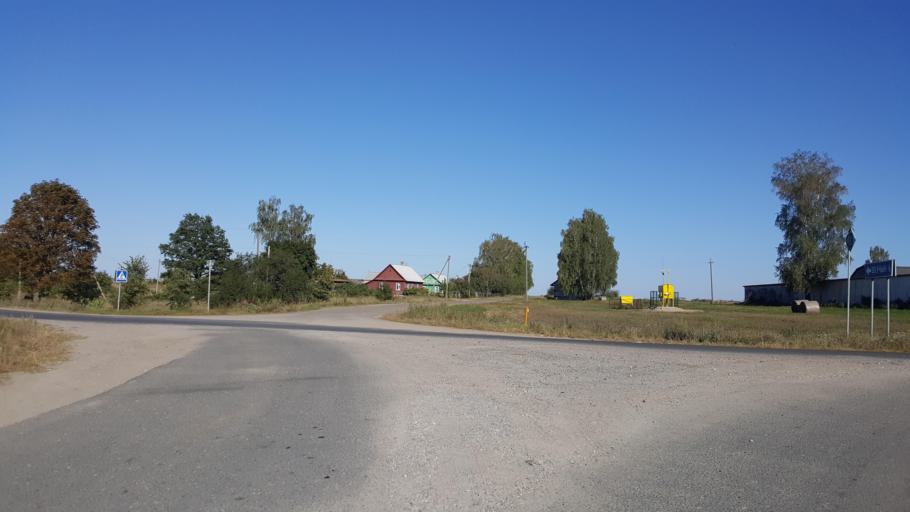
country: PL
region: Lublin Voivodeship
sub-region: Powiat bialski
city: Janow Podlaski
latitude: 52.2608
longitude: 23.2348
